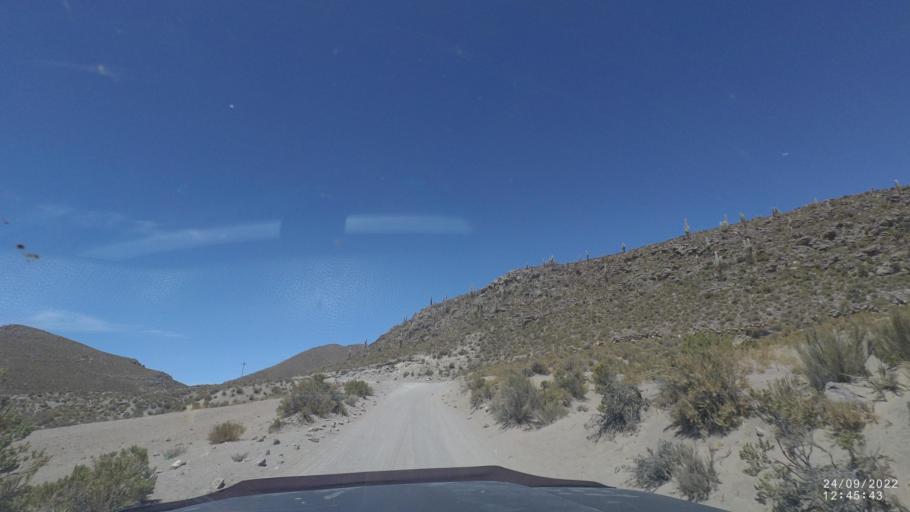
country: BO
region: Potosi
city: Colchani
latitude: -19.8005
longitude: -67.5754
